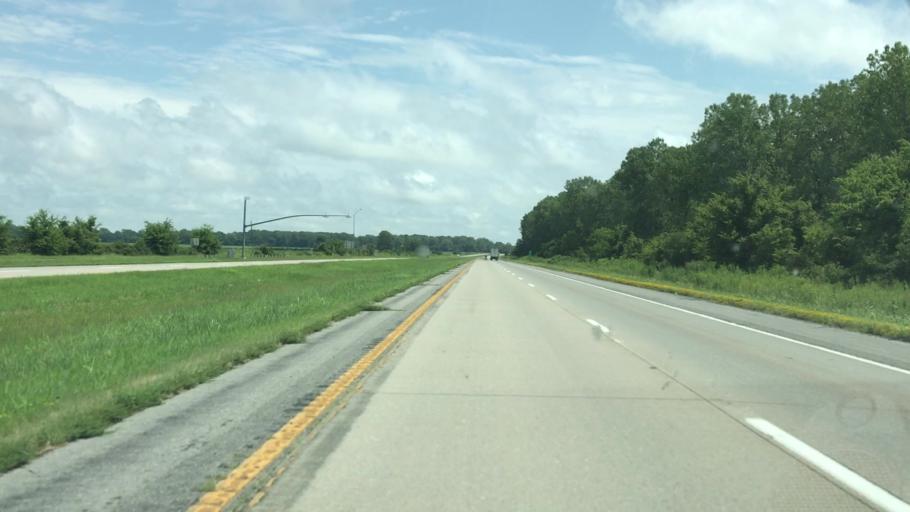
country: US
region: Missouri
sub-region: Pemiscot County
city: Caruthersville
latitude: 36.1426
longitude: -89.6434
